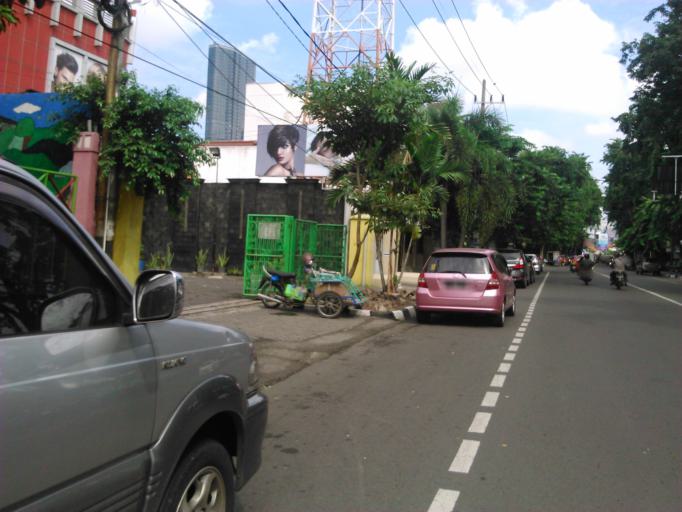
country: ID
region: East Java
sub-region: Kota Surabaya
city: Surabaya
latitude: -7.2605
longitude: 112.7457
